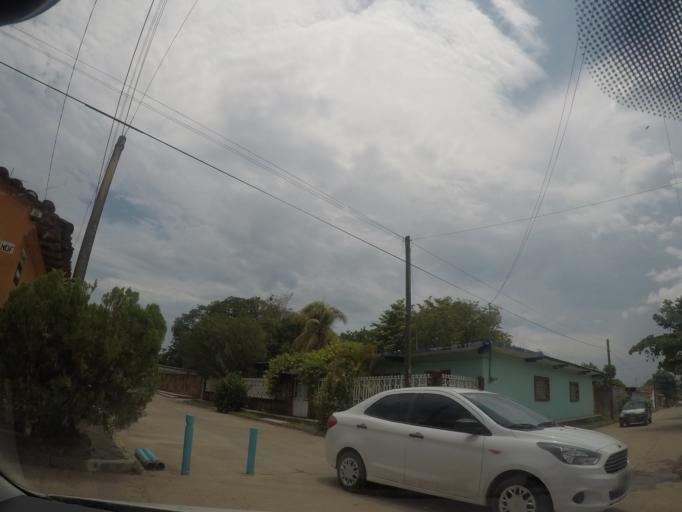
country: MX
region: Oaxaca
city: Santo Domingo Zanatepec
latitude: 16.4839
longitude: -94.3536
